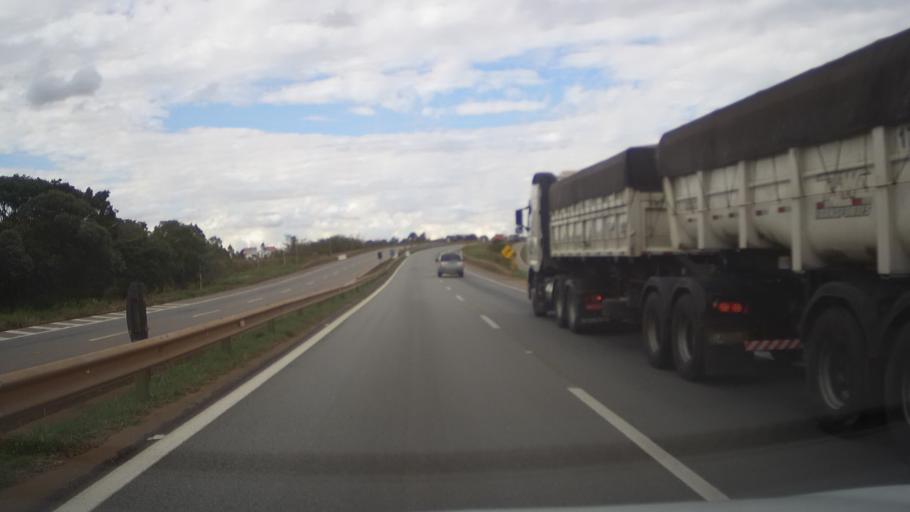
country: BR
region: Minas Gerais
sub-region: Itauna
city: Itauna
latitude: -20.3064
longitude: -44.4476
